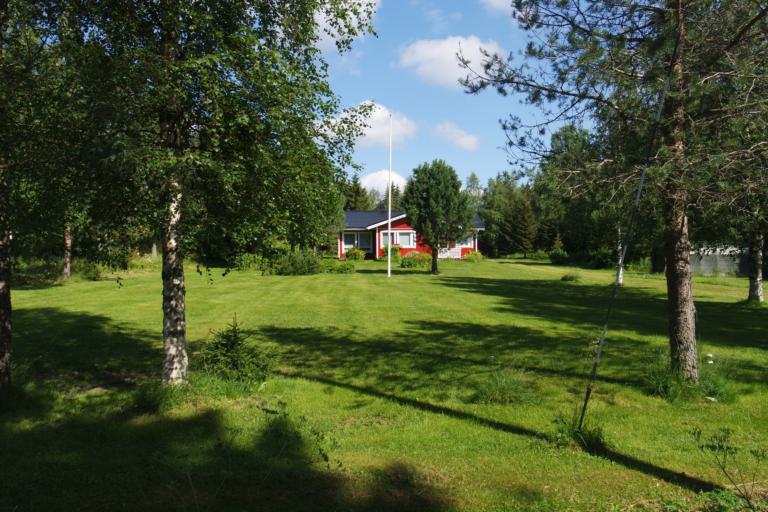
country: FI
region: Lapland
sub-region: Kemi-Tornio
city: Tornio
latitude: 65.9632
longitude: 24.0447
